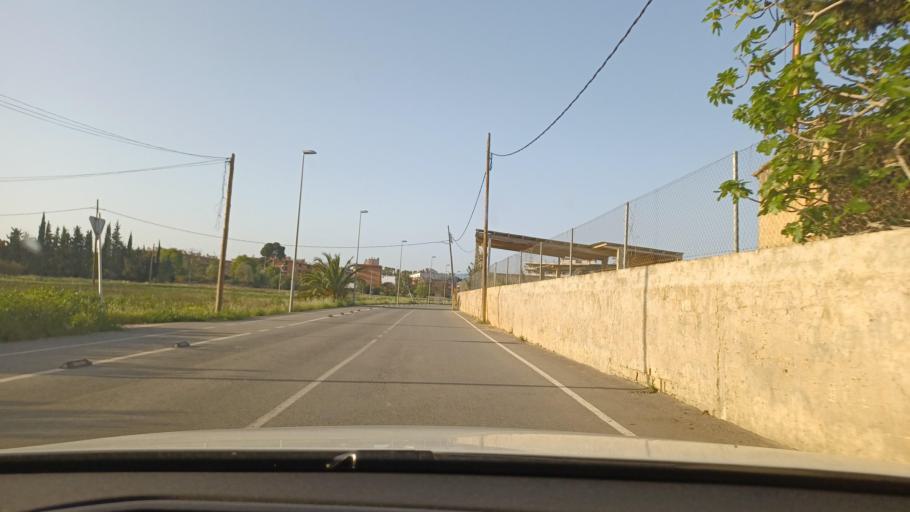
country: ES
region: Catalonia
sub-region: Provincia de Tarragona
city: Tortosa
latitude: 40.8002
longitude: 0.5181
